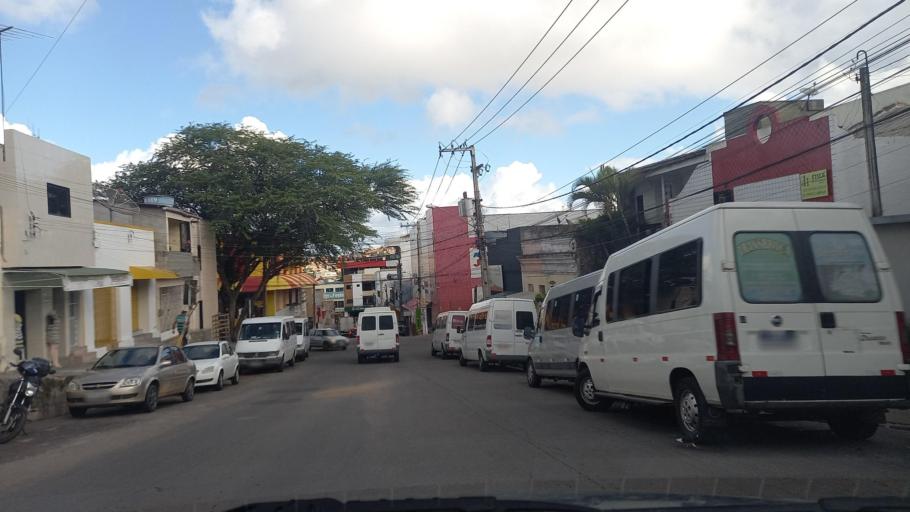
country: BR
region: Pernambuco
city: Garanhuns
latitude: -8.8888
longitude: -36.4963
